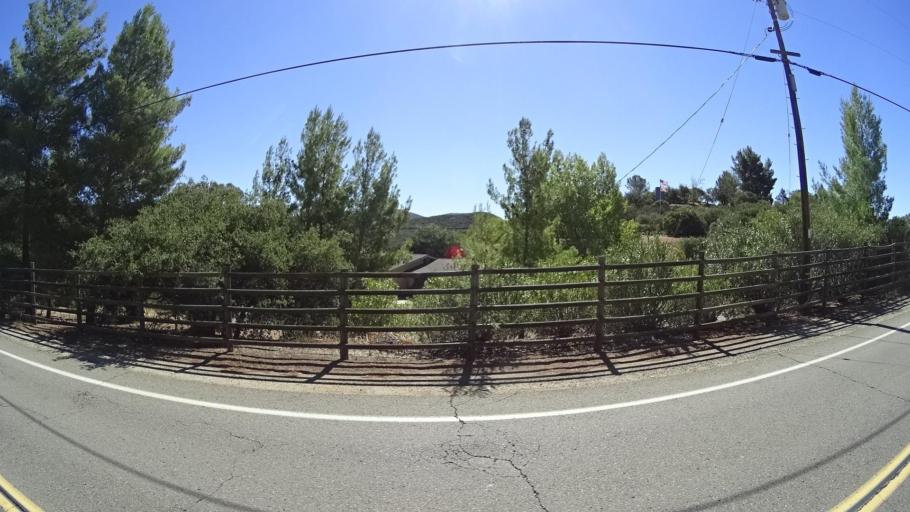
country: US
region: California
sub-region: San Diego County
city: Descanso
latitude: 32.8032
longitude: -116.6421
